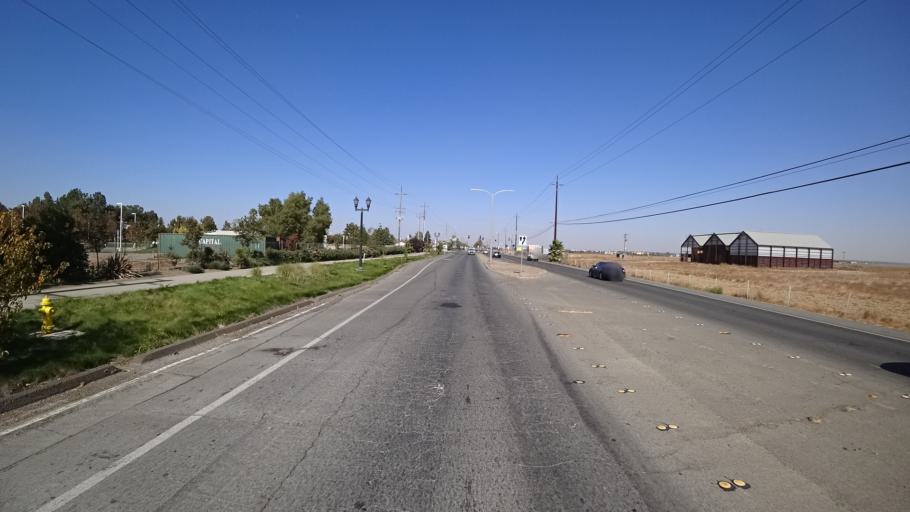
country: US
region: California
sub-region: Yolo County
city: Woodland
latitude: 38.6612
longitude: -121.7287
